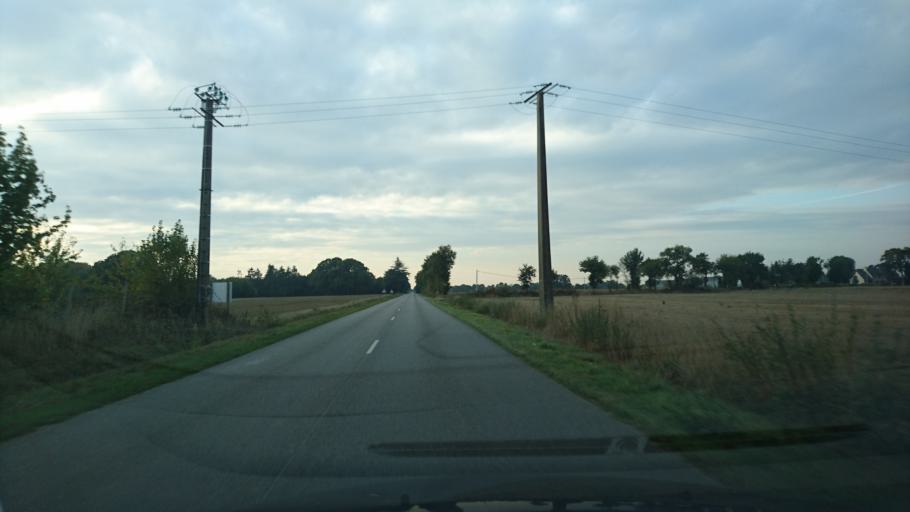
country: FR
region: Brittany
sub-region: Departement du Morbihan
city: Saint-Vincent-sur-Oust
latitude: 47.7059
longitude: -2.1596
